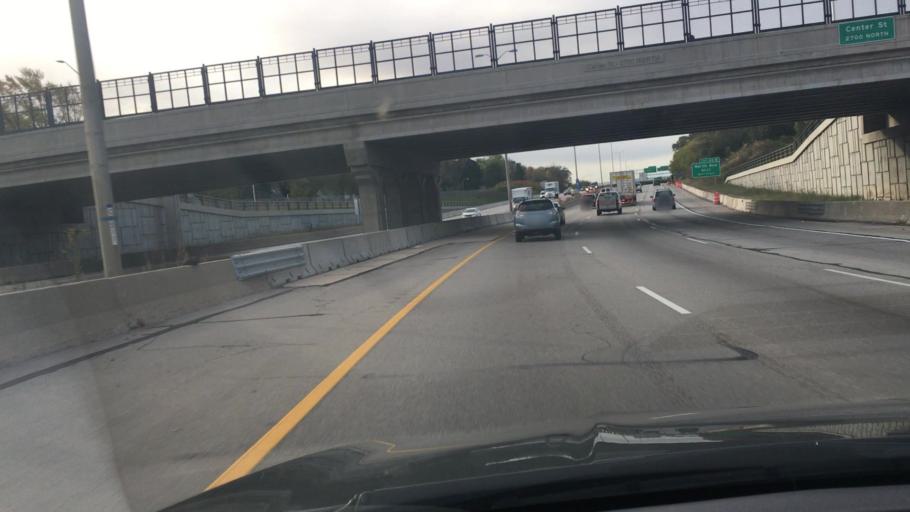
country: US
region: Wisconsin
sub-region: Waukesha County
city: Elm Grove
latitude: 43.0678
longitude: -88.0535
